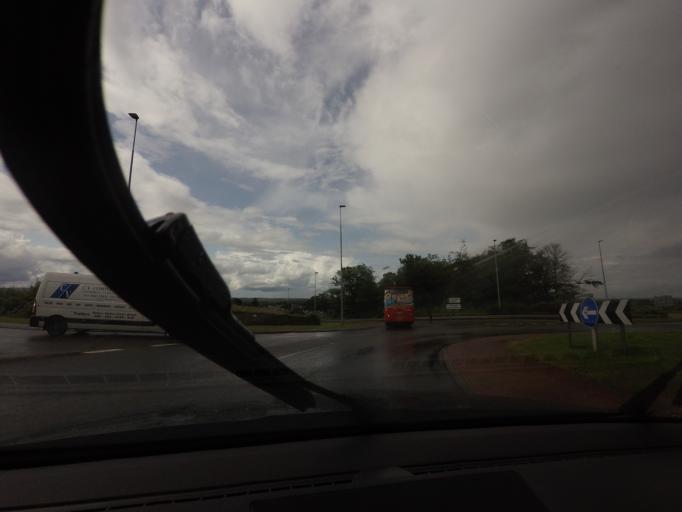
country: GB
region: Scotland
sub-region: Moray
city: Fochabers
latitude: 57.6108
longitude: -3.0847
